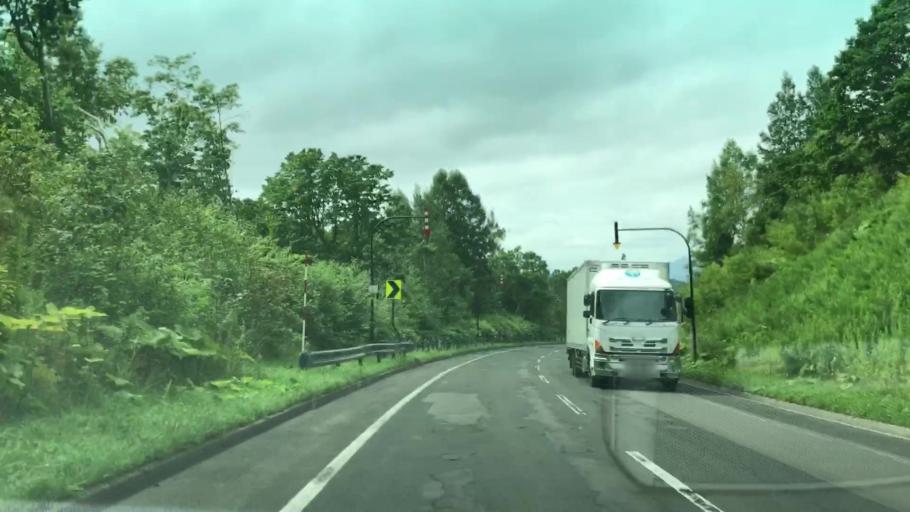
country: JP
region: Hokkaido
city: Yoichi
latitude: 42.9567
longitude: 140.8690
